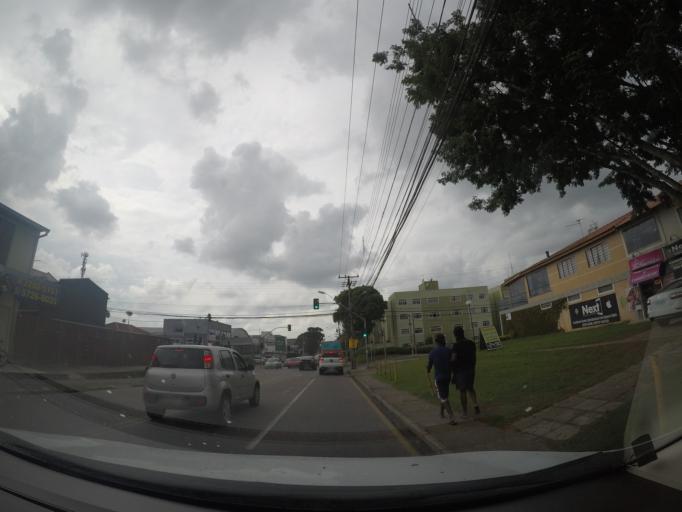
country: BR
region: Parana
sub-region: Sao Jose Dos Pinhais
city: Sao Jose dos Pinhais
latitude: -25.5230
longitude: -49.2424
